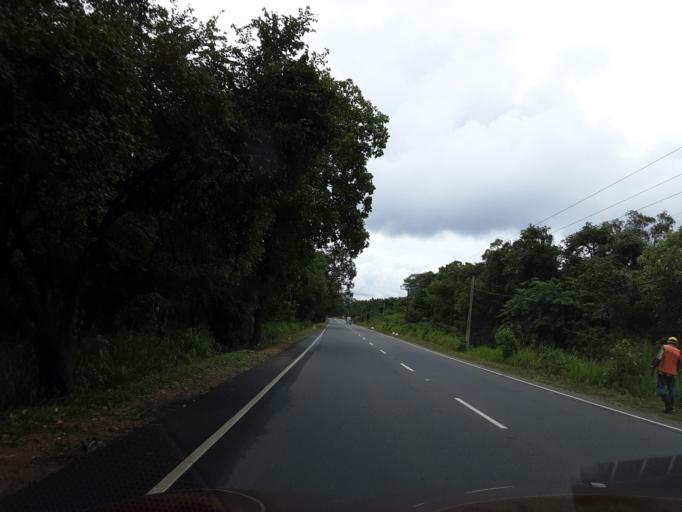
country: LK
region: Uva
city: Badulla
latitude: 7.3988
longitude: 81.1060
